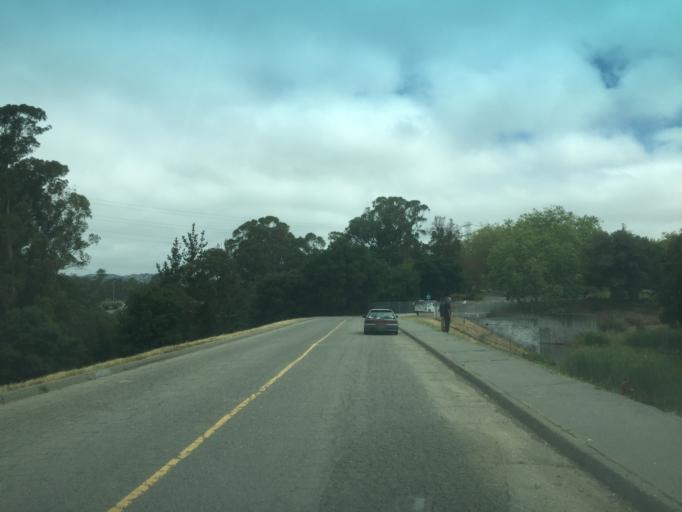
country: US
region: California
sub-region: Alameda County
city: Fairview
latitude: 37.6903
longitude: -122.0556
